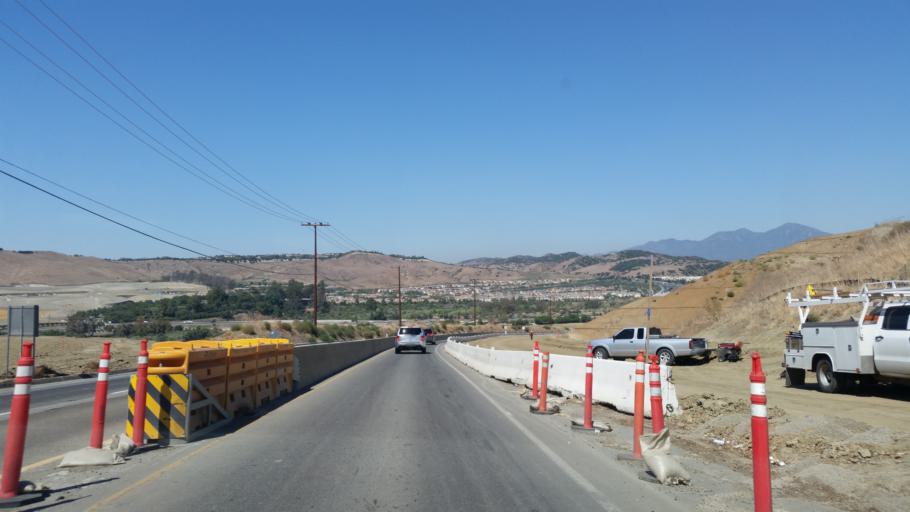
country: US
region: California
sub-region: Orange County
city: San Juan Capistrano
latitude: 33.5117
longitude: -117.6227
